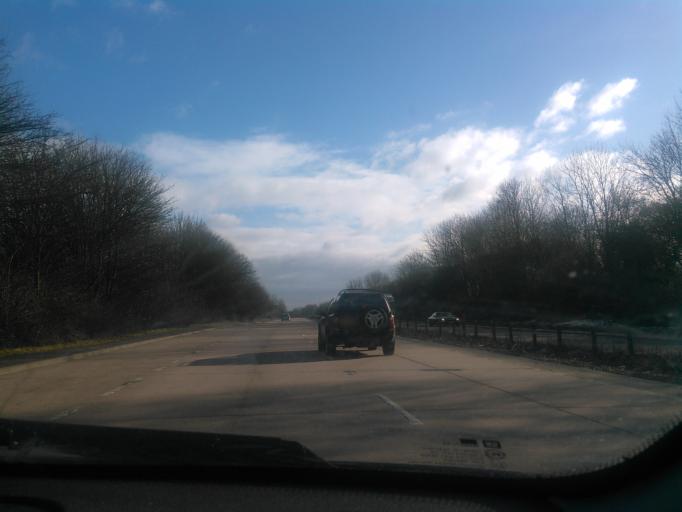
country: GB
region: England
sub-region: Staffordshire
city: Uttoxeter
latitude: 52.9192
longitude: -1.9169
